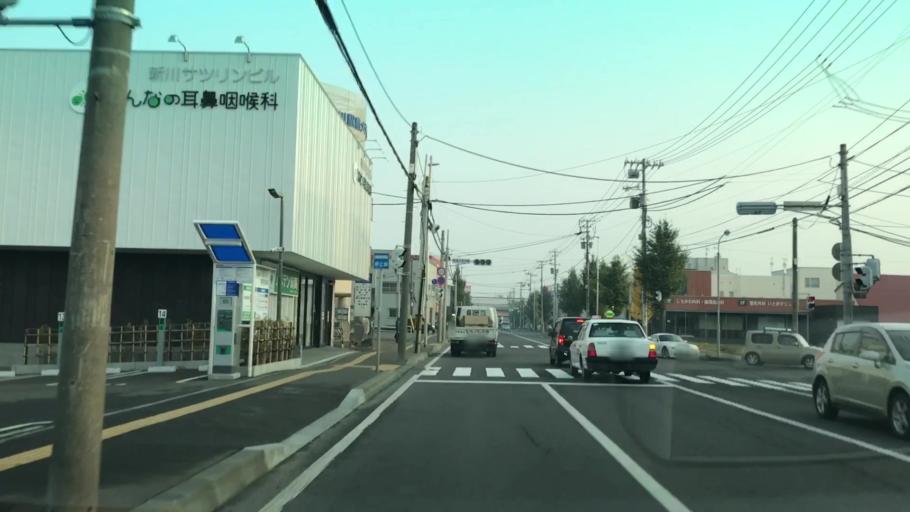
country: JP
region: Hokkaido
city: Sapporo
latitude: 43.0985
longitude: 141.3253
